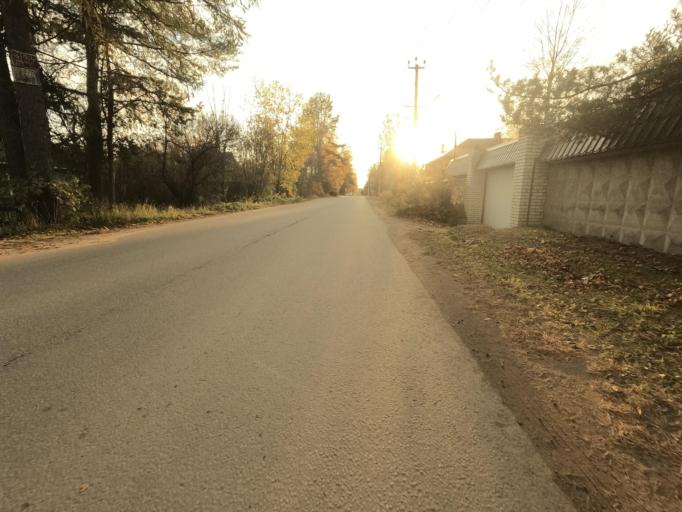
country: RU
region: St.-Petersburg
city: Beloostrov
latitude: 60.1755
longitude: 30.0232
